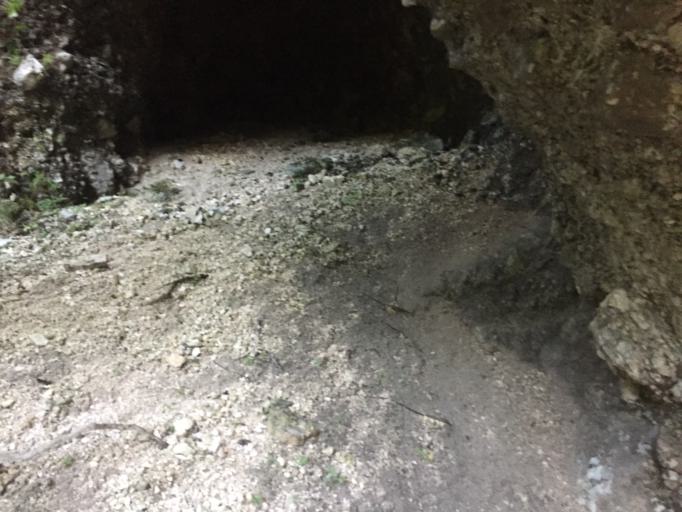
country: IT
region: Friuli Venezia Giulia
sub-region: Provincia di Udine
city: Resiutta
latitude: 46.3481
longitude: 13.1930
